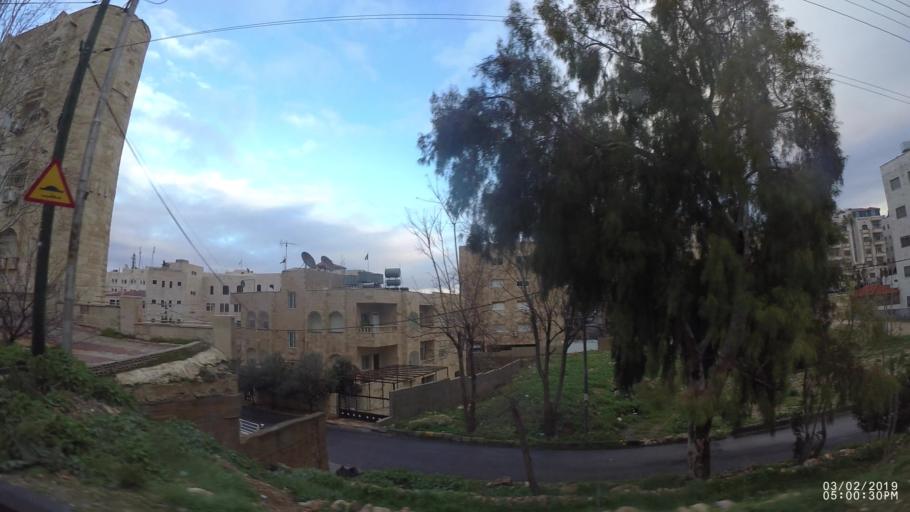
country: JO
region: Amman
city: Amman
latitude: 31.9794
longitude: 35.9140
